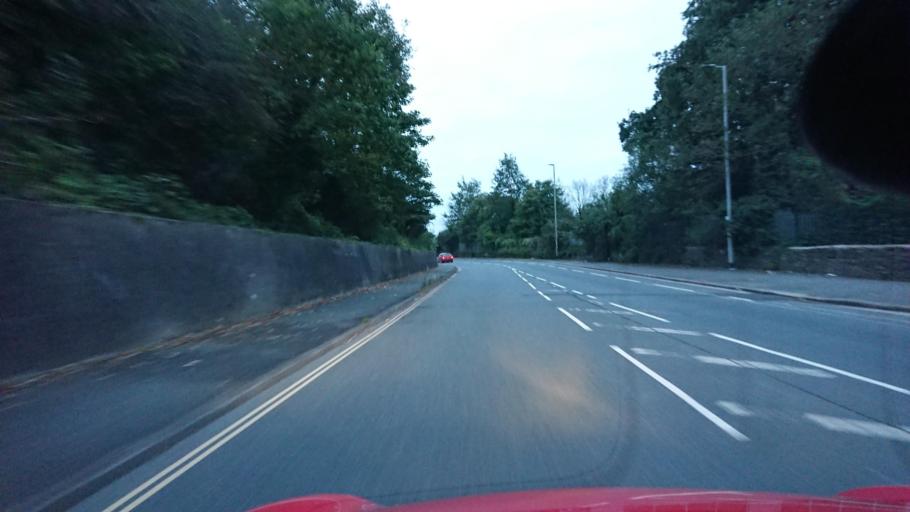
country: GB
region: England
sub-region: Cornwall
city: Torpoint
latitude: 50.3991
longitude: -4.1834
